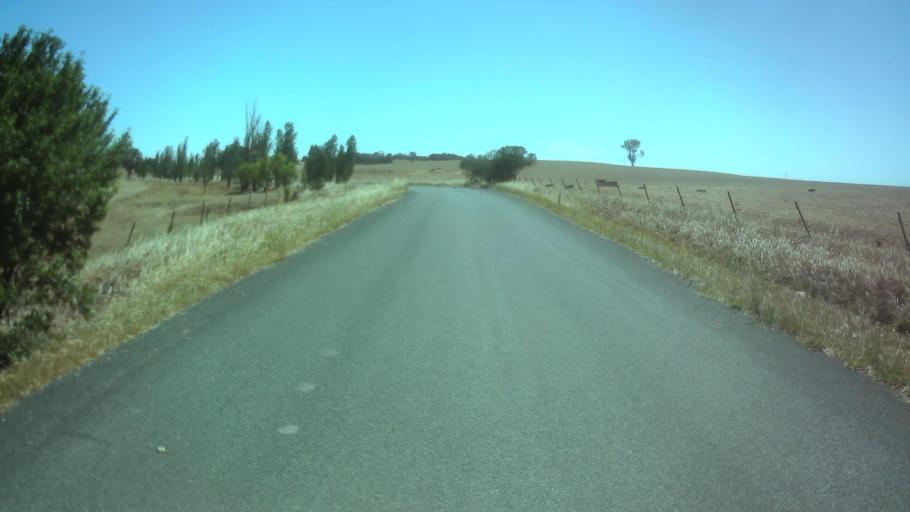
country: AU
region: New South Wales
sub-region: Weddin
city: Grenfell
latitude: -33.9769
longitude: 148.4027
